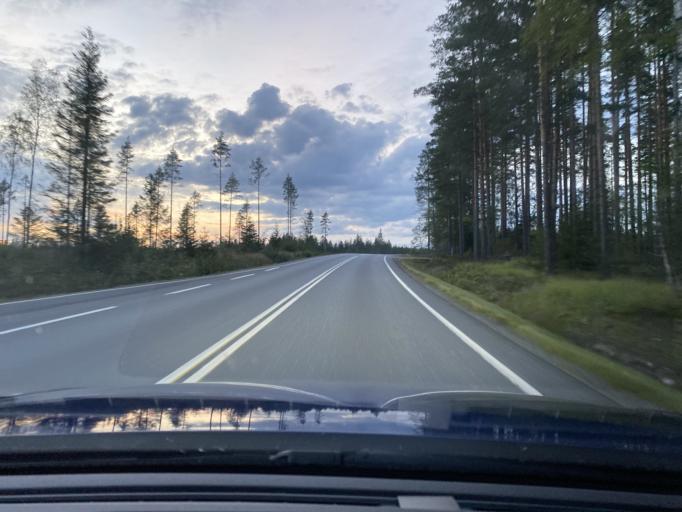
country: FI
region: Southern Ostrobothnia
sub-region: Suupohja
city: Kauhajoki
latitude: 62.2277
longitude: 22.2729
